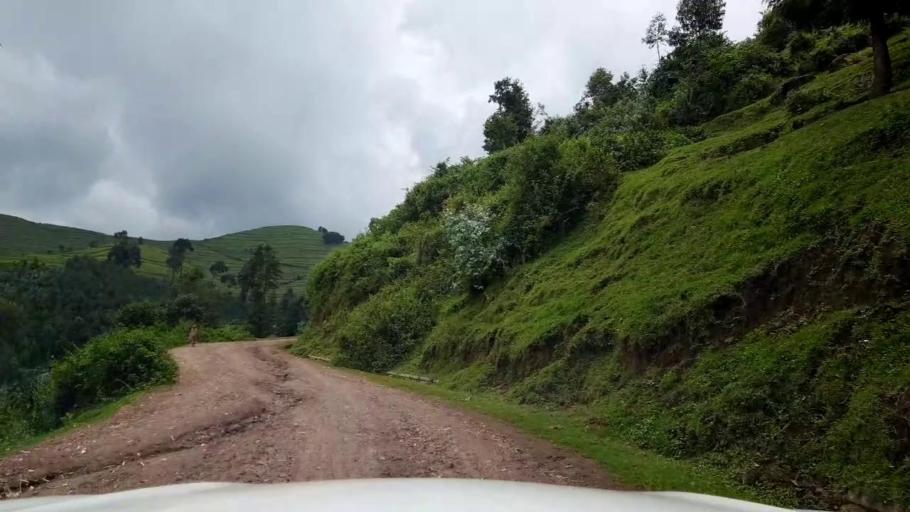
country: RW
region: Western Province
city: Gisenyi
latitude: -1.6489
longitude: 29.4116
